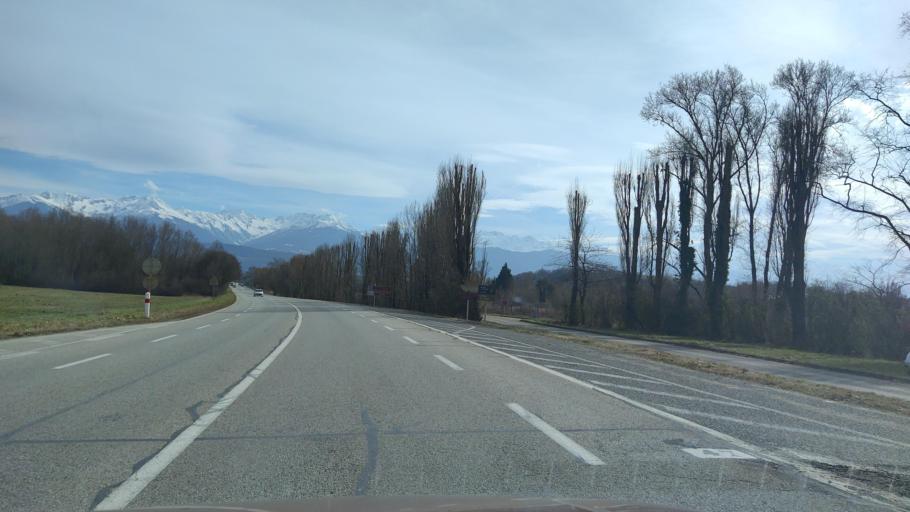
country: FR
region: Rhone-Alpes
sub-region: Departement de la Savoie
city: Les Marches
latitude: 45.5221
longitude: 5.9957
